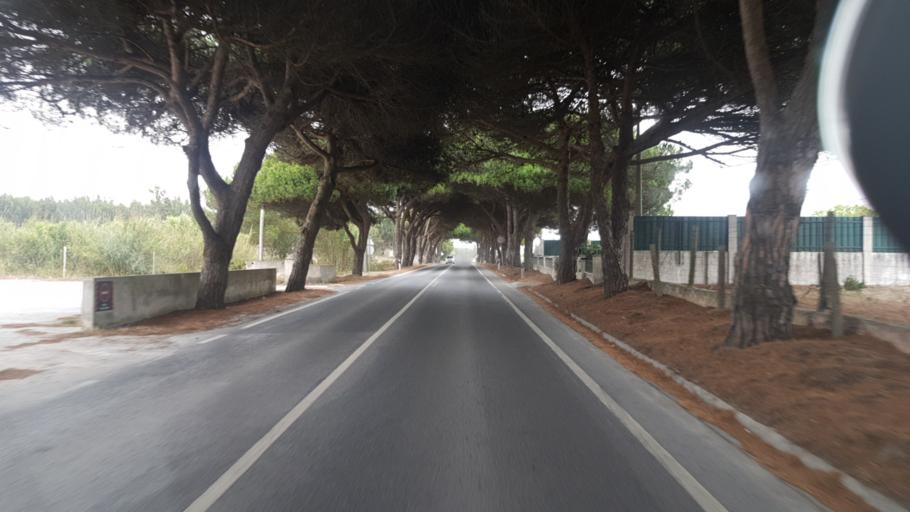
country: PT
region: Lisbon
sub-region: Torres Vedras
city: Silveira
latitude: 39.0926
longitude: -9.3434
